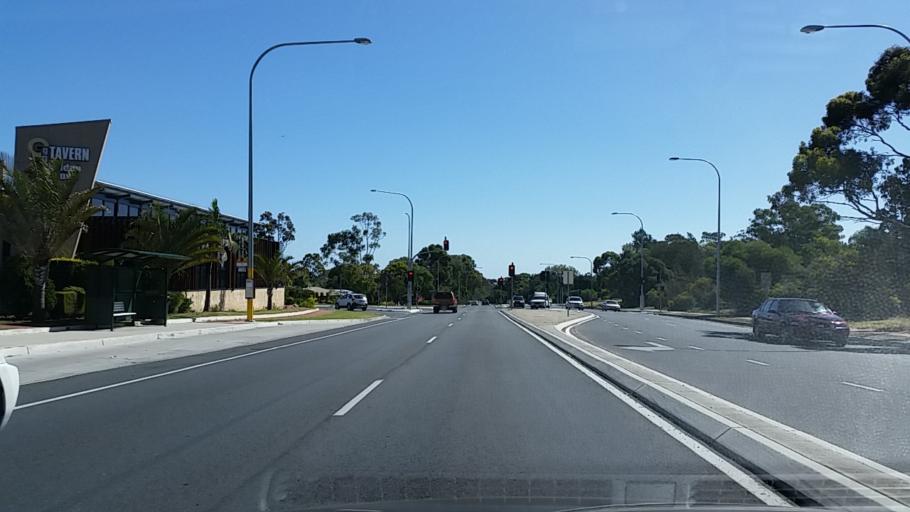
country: AU
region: South Australia
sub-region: Tea Tree Gully
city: Hope Valley
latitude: -34.8056
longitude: 138.7012
